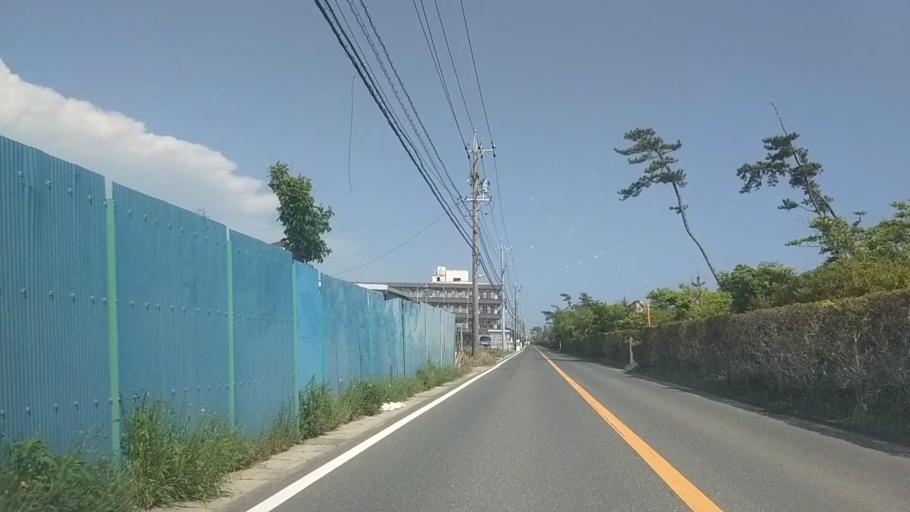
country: JP
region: Shizuoka
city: Hamamatsu
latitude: 34.6668
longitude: 137.7206
